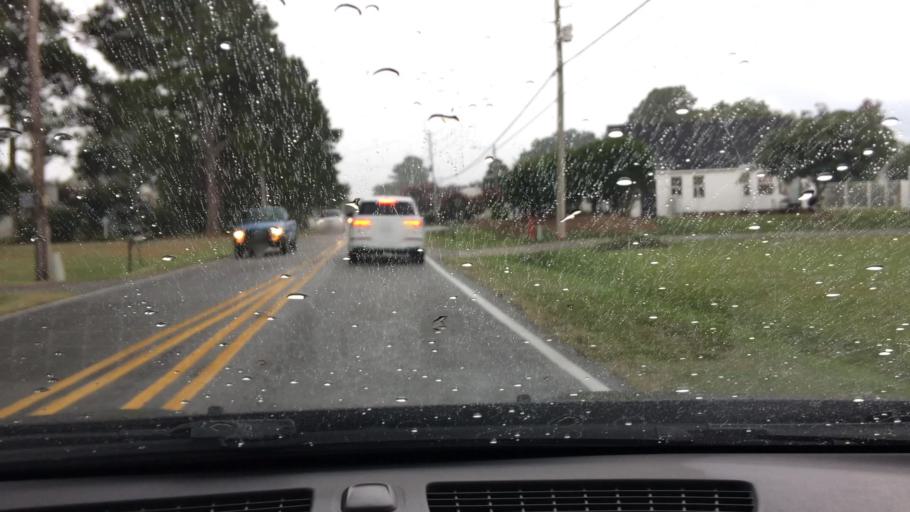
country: US
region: North Carolina
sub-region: Pitt County
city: Winterville
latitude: 35.5347
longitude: -77.3848
